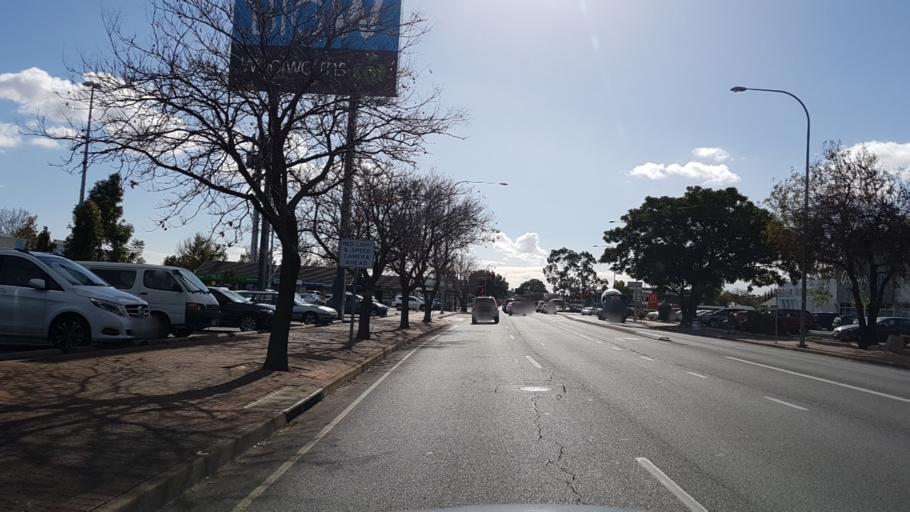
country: AU
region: South Australia
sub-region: Unley
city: Millswood
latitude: -34.9677
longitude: 138.5908
